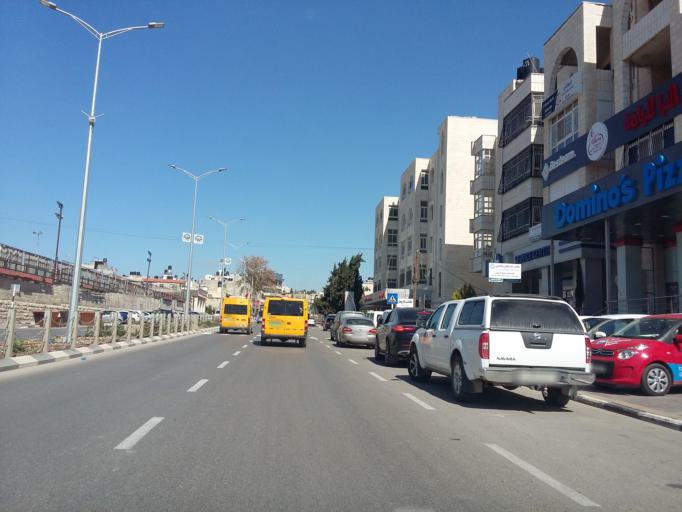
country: PS
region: West Bank
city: Ramallah
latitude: 31.8925
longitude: 35.2141
